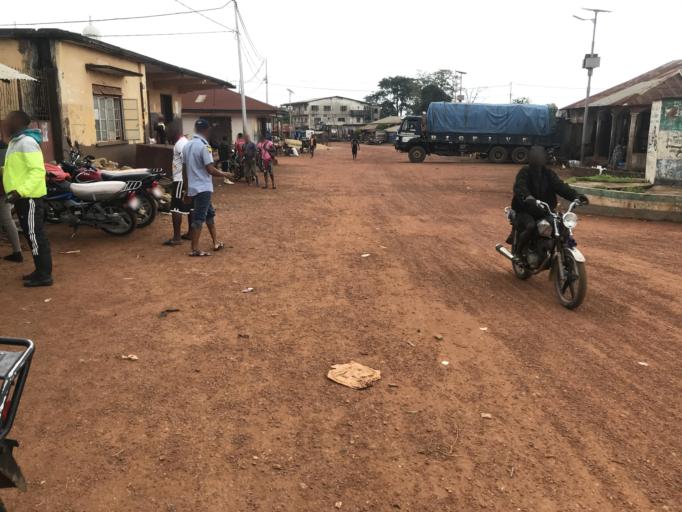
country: SL
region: Eastern Province
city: Buedu
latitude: 8.4618
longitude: -10.3382
